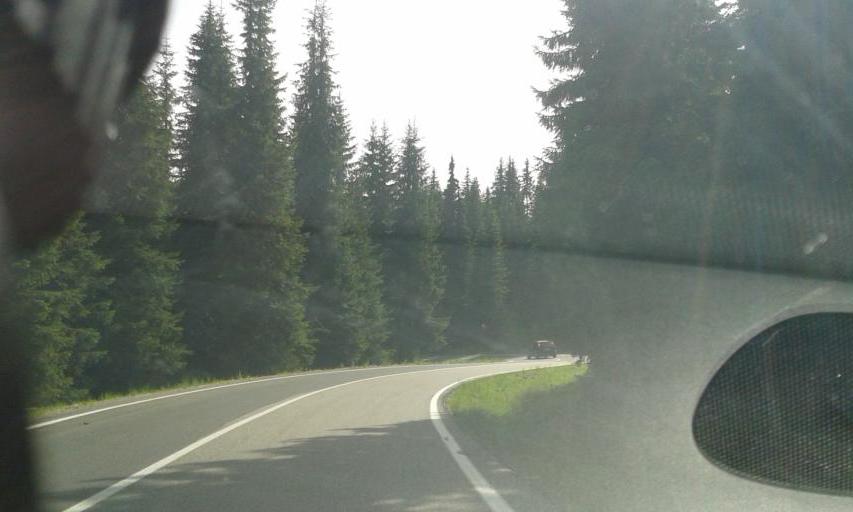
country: RO
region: Hunedoara
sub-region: Oras Petrila
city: Petrila
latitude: 45.4686
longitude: 23.6312
